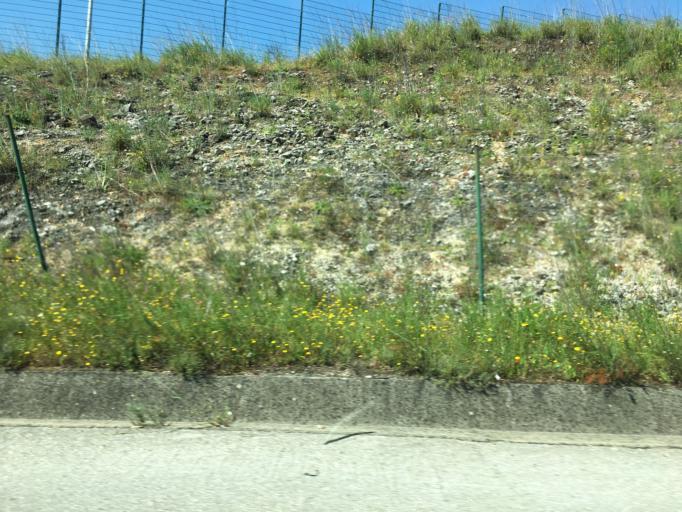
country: PT
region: Lisbon
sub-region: Odivelas
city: Famoes
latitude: 38.7777
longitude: -9.2276
